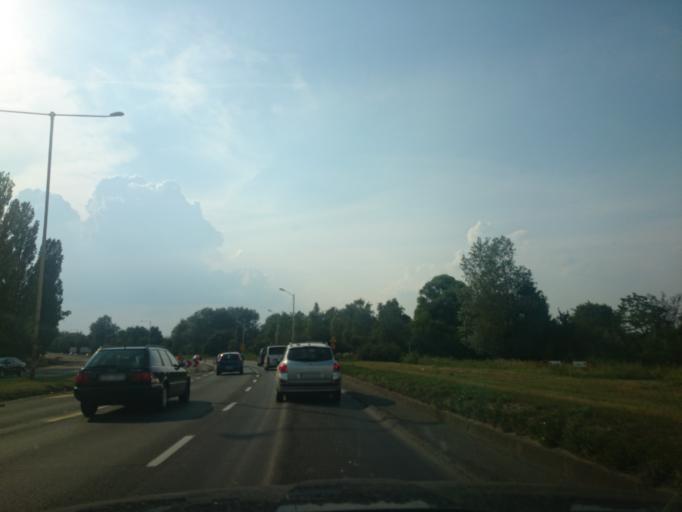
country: PL
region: West Pomeranian Voivodeship
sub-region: Szczecin
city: Szczecin
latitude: 53.3864
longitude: 14.6410
